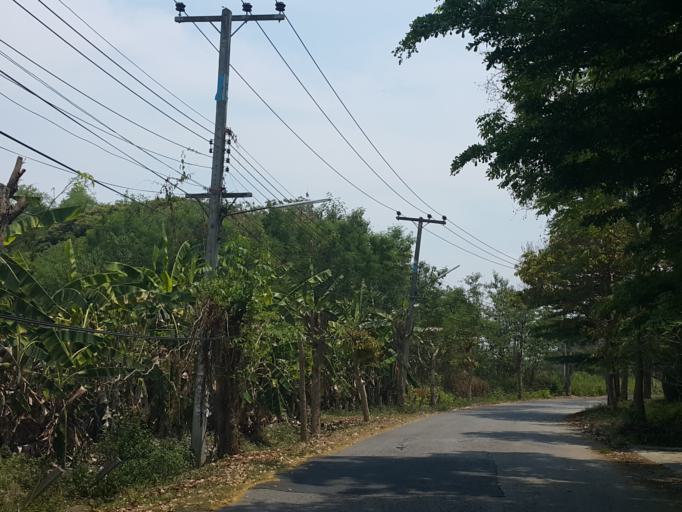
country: TH
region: Chiang Mai
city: Chiang Mai
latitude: 18.7329
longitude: 98.9771
